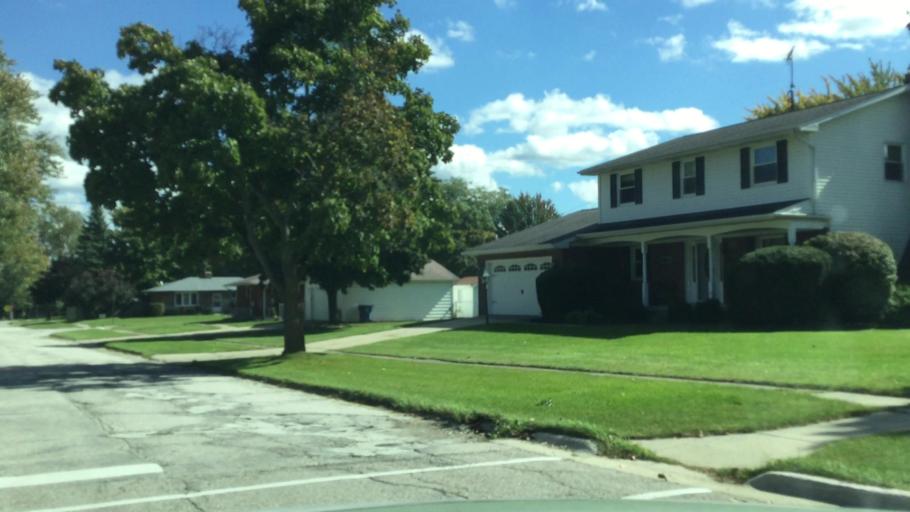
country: US
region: Michigan
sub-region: Genesee County
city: Swartz Creek
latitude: 42.9497
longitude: -83.8562
